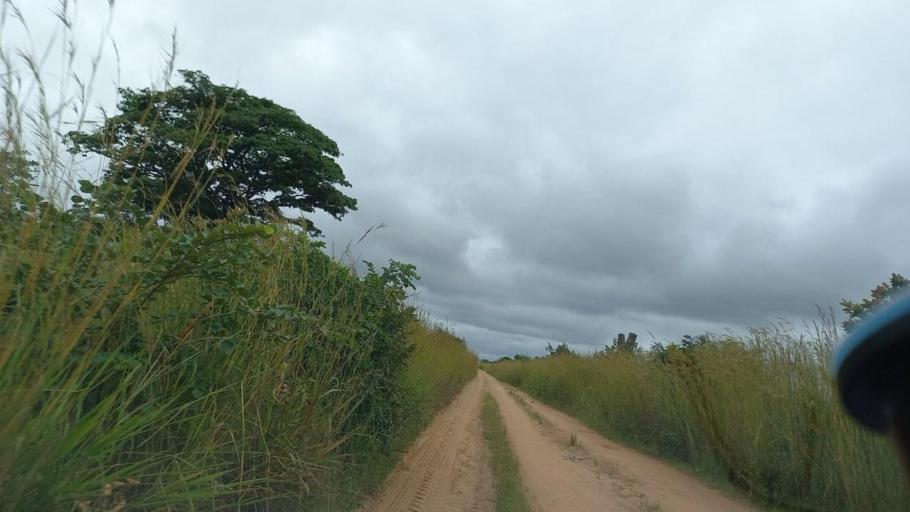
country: ZM
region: Lusaka
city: Lusaka
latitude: -15.1361
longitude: 28.3682
